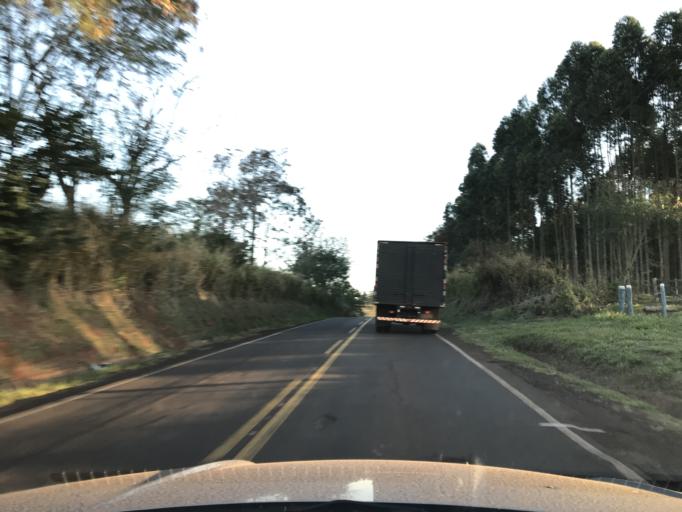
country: PY
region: Canindeyu
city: Salto del Guaira
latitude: -24.0963
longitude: -54.0987
